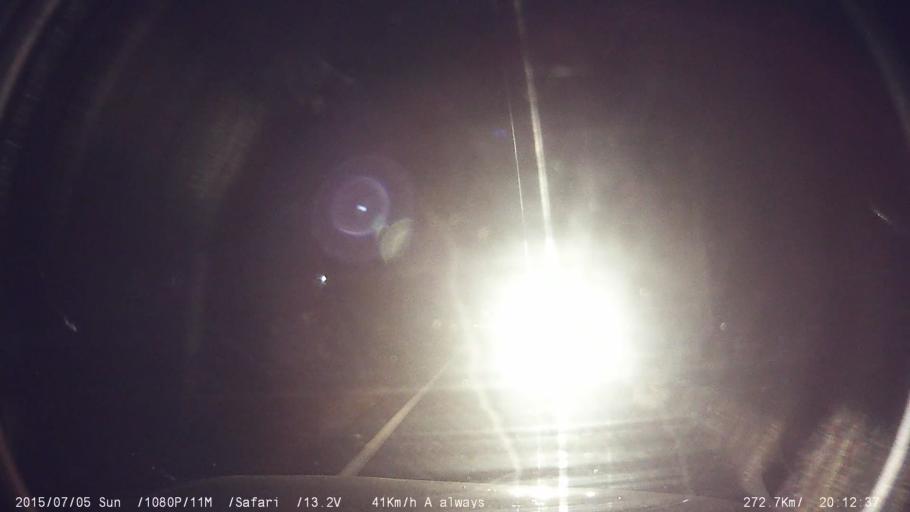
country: IN
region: Kerala
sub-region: Palakkad district
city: Palakkad
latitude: 10.8610
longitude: 76.5630
